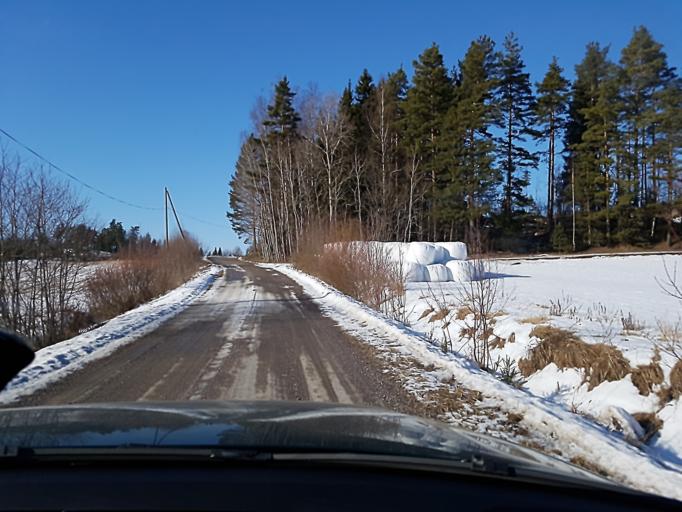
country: FI
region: Uusimaa
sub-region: Helsinki
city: Karjalohja
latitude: 60.2119
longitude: 23.7012
